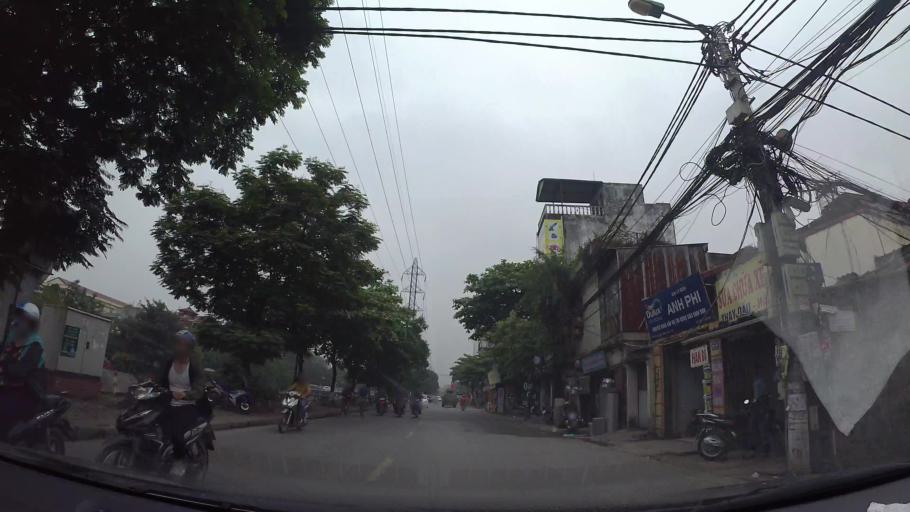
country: VN
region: Ha Noi
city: Hai BaTrung
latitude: 20.9900
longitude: 105.8632
